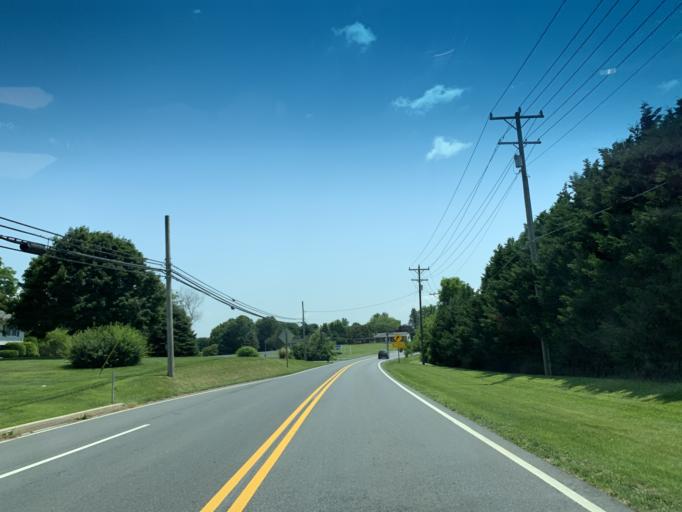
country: US
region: Maryland
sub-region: Frederick County
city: Green Valley
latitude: 39.3636
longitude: -77.2695
